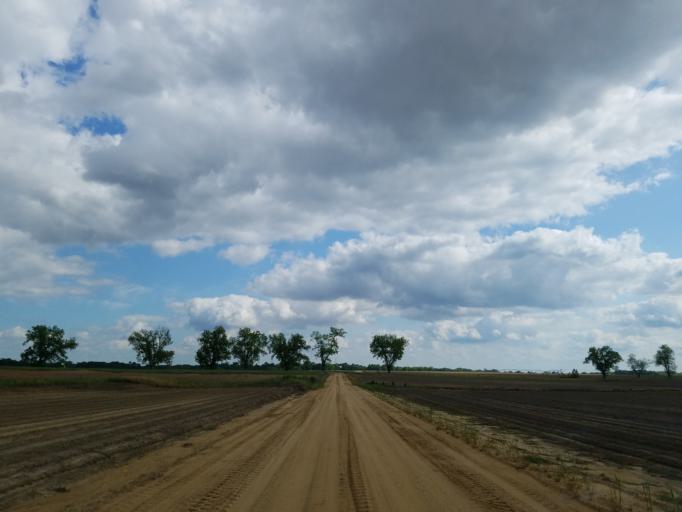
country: US
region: Georgia
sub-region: Dooly County
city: Vienna
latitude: 32.1684
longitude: -83.7759
